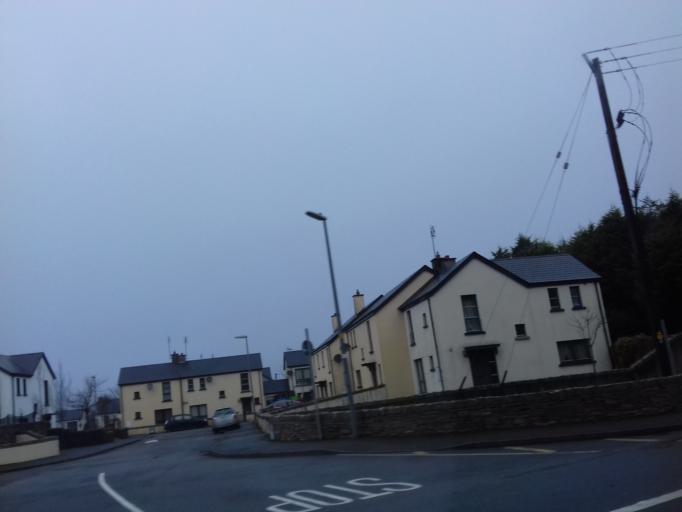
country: IE
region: Ulster
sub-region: County Donegal
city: Ramelton
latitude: 55.0327
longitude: -7.6473
